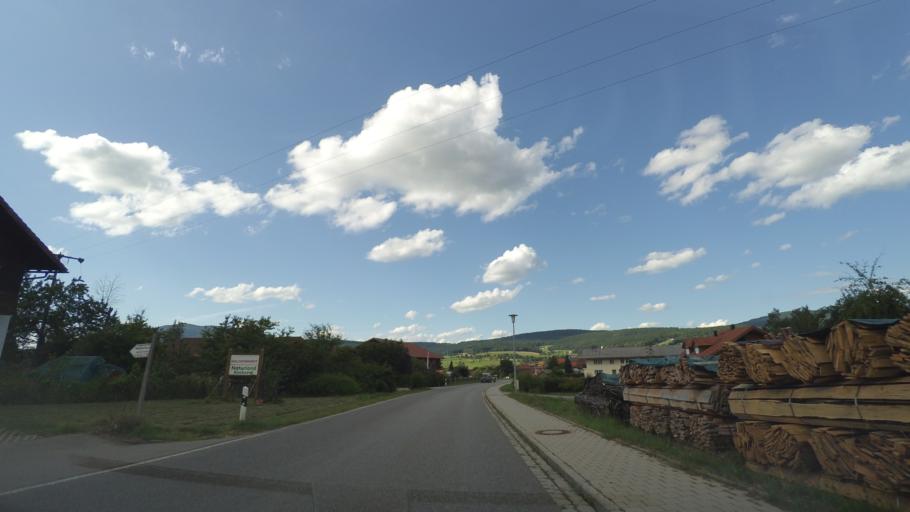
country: DE
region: Bavaria
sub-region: Upper Palatinate
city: Arrach
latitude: 49.1910
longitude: 13.0029
